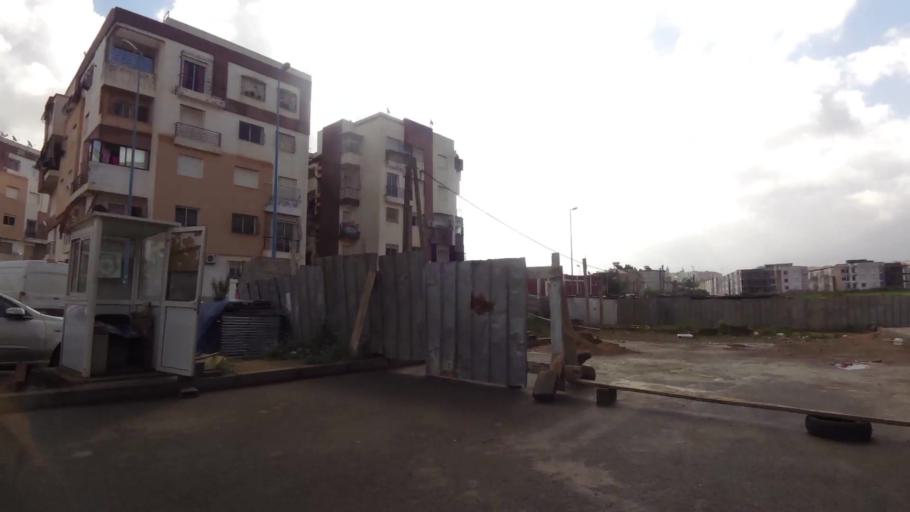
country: MA
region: Grand Casablanca
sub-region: Casablanca
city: Casablanca
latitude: 33.5384
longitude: -7.6925
